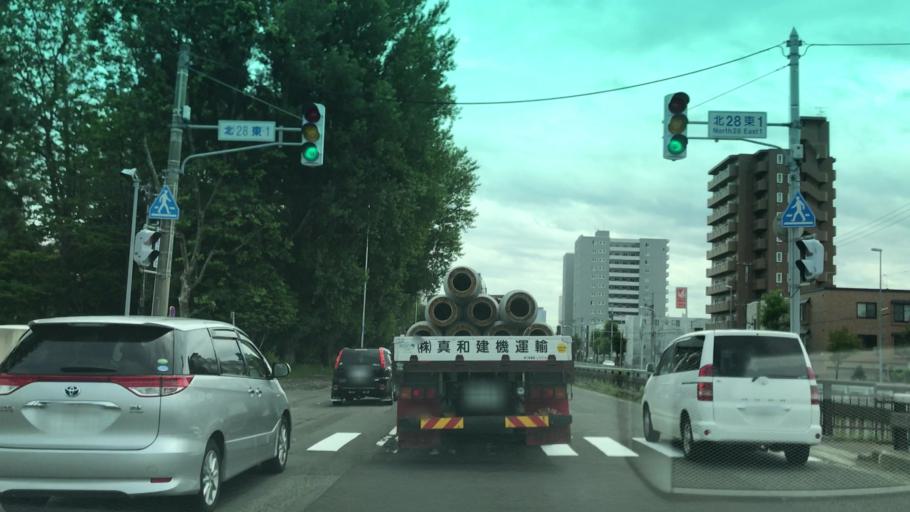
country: JP
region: Hokkaido
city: Sapporo
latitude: 43.0955
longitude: 141.3466
